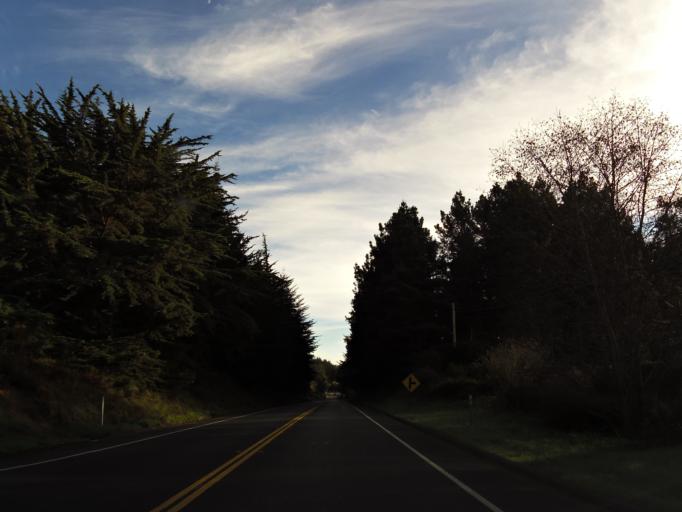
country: US
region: California
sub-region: Mendocino County
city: Fort Bragg
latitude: 39.3230
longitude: -123.8019
